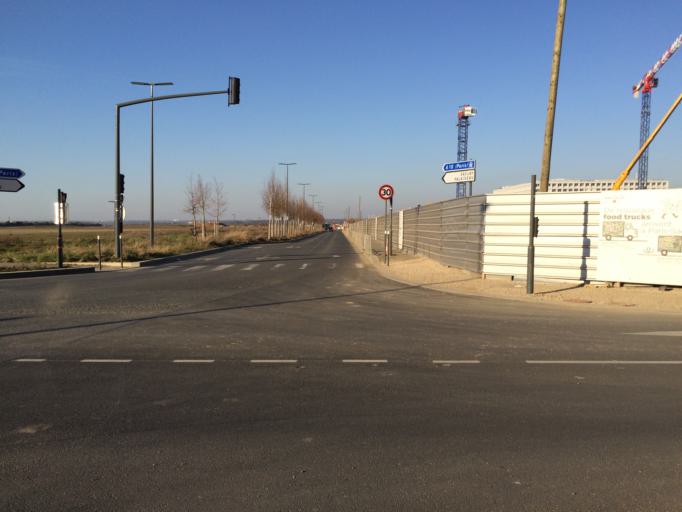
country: FR
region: Ile-de-France
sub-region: Departement de l'Essonne
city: Orsay
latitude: 48.7132
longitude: 2.1922
